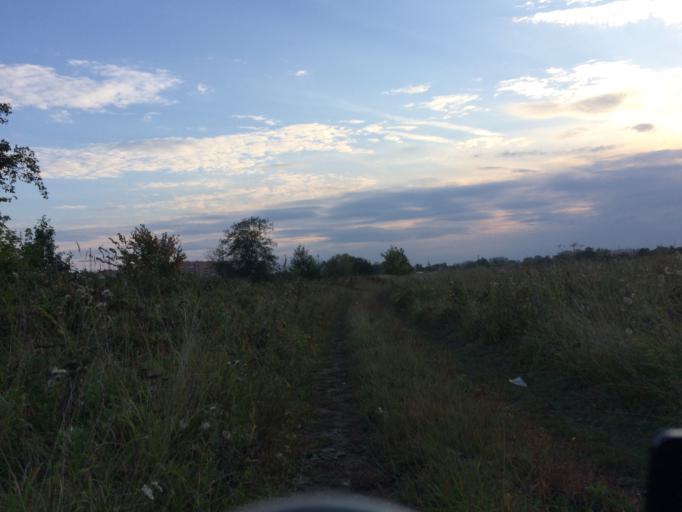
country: RU
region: Mariy-El
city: Yoshkar-Ola
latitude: 56.6479
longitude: 47.9253
